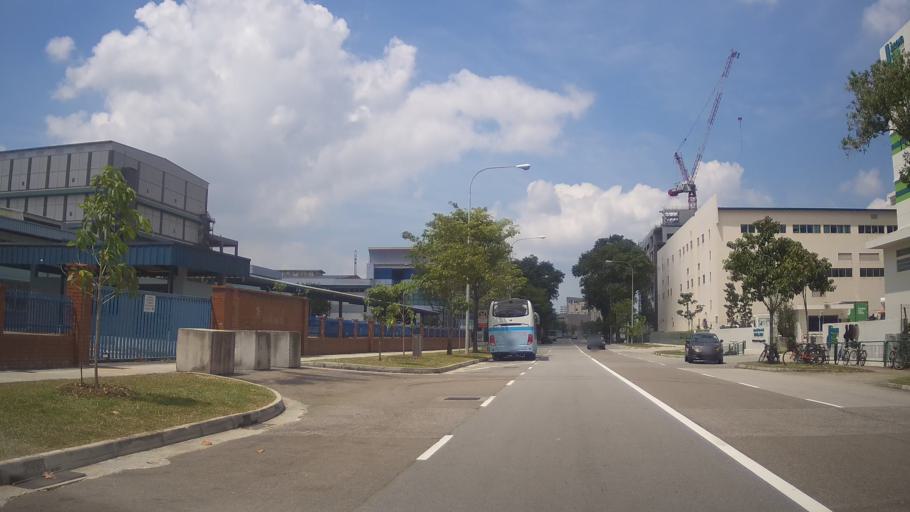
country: MY
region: Johor
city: Johor Bahru
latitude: 1.3367
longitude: 103.7160
